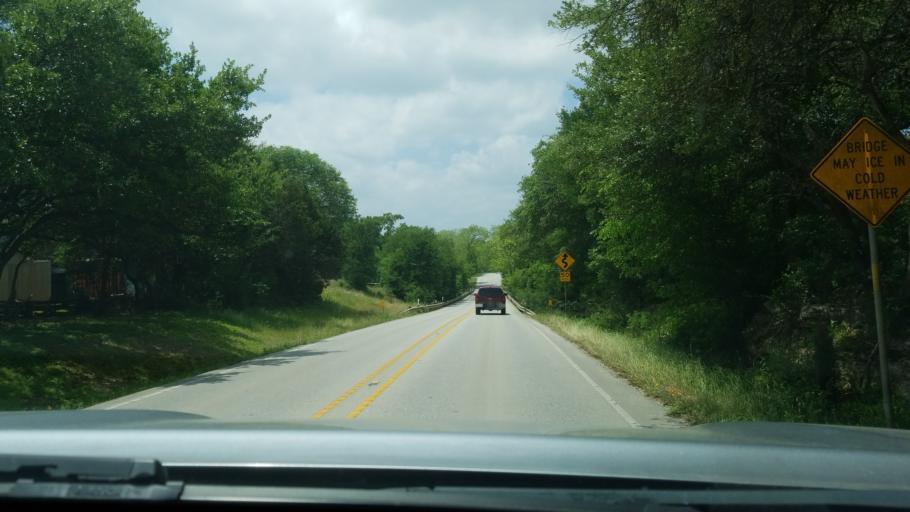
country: US
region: Texas
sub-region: Hays County
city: Dripping Springs
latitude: 30.1313
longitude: -98.0145
